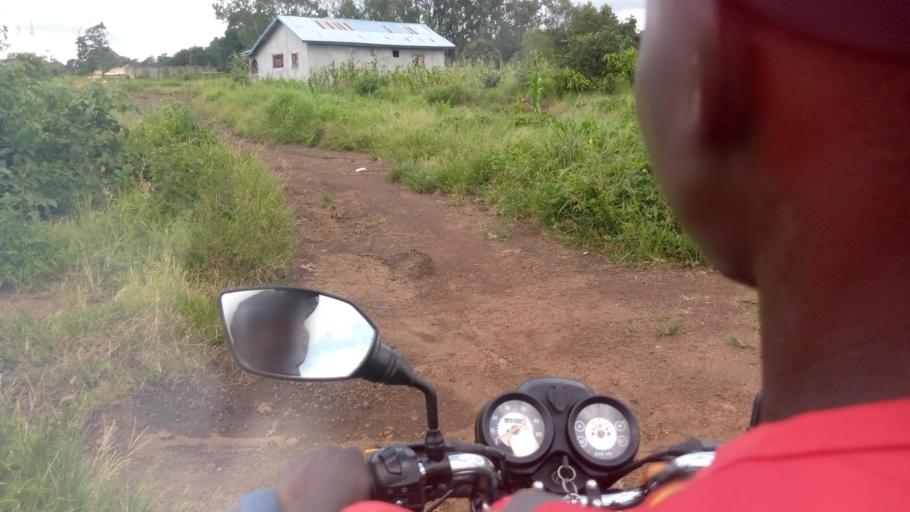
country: SL
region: Northern Province
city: Kamakwie
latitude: 9.4905
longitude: -12.2331
